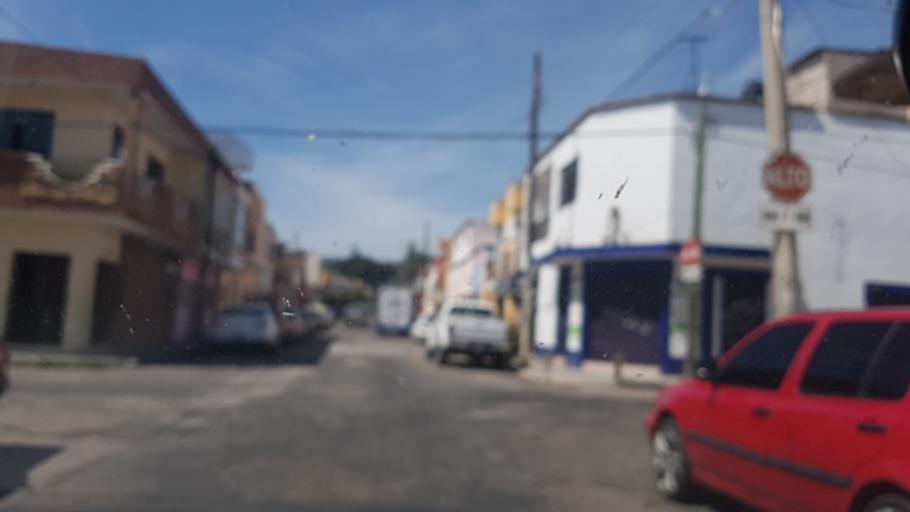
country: MX
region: Nayarit
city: Tepic
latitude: 21.5083
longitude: -104.8978
